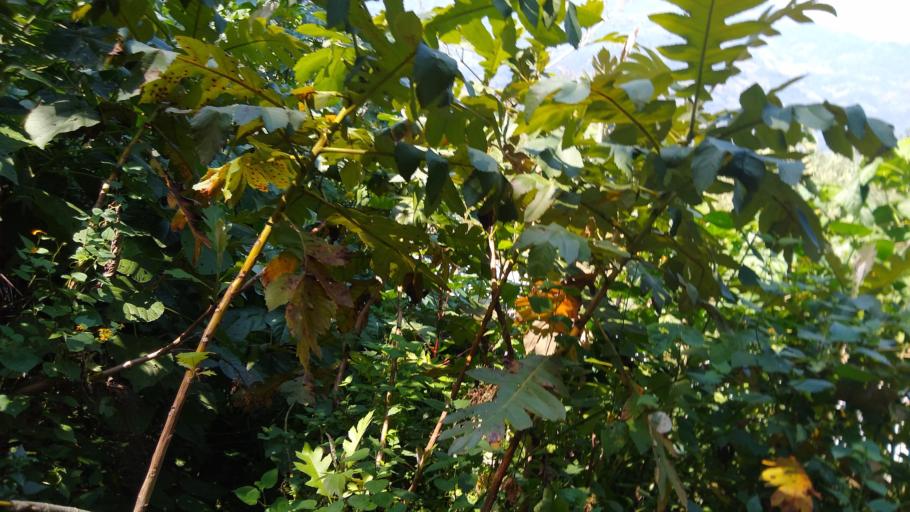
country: MX
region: Puebla
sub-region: Tepetzintla
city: Tlamanca de Hernandez
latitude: 19.9322
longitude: -97.8096
